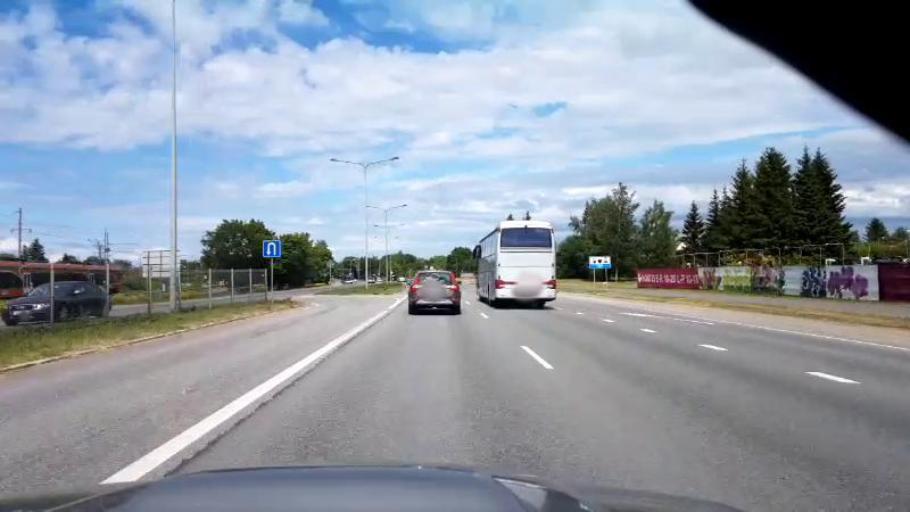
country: EE
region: Harju
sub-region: Saue vald
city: Laagri
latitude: 59.3492
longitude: 24.6265
